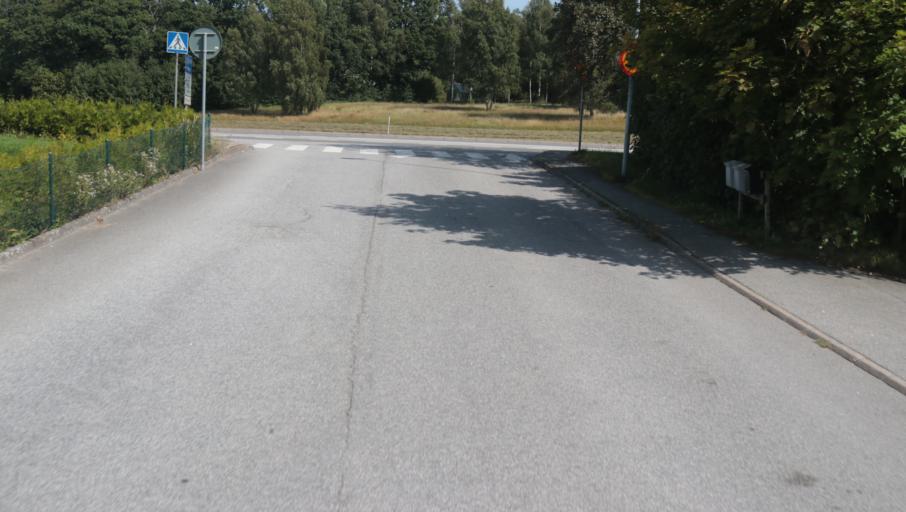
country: SE
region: Blekinge
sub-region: Karlshamns Kommun
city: Karlshamn
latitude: 56.1980
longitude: 14.8373
